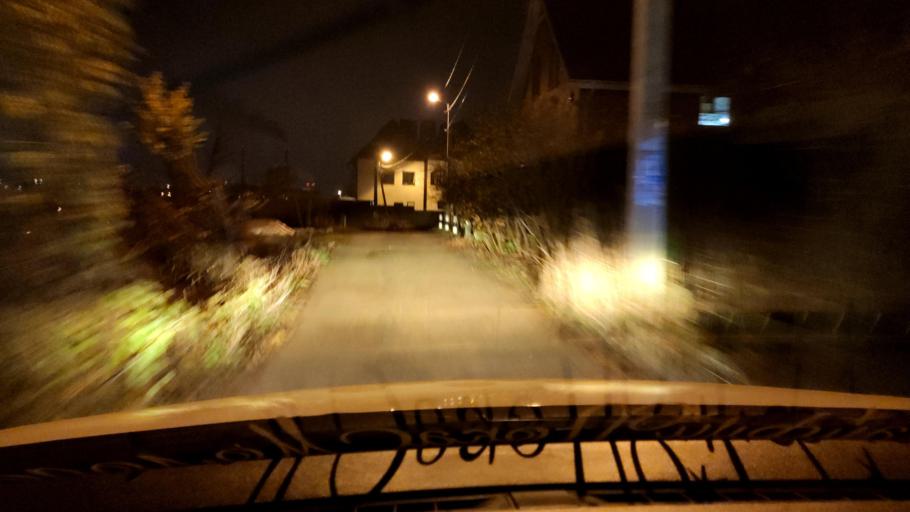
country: RU
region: Voronezj
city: Voronezh
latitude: 51.6259
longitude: 39.1954
